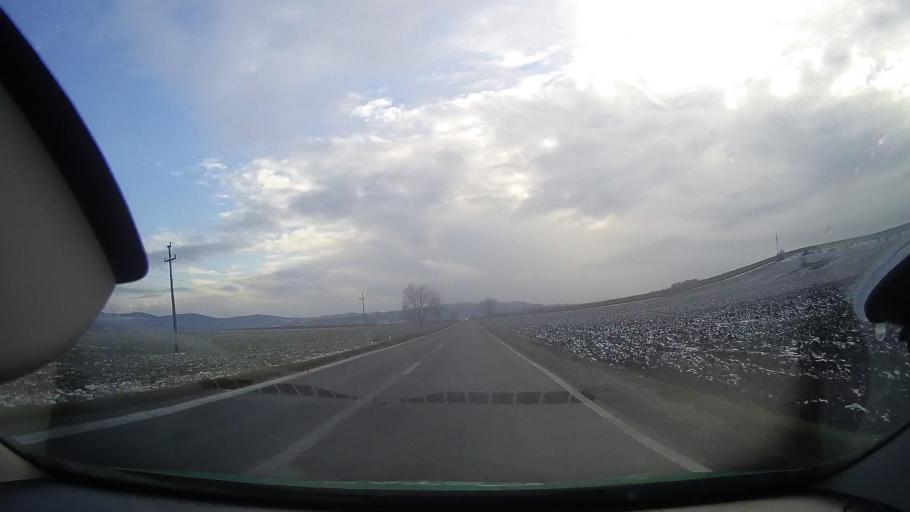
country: RO
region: Mures
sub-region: Comuna Cucerdea
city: Cucerdea
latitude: 46.4146
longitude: 24.2639
